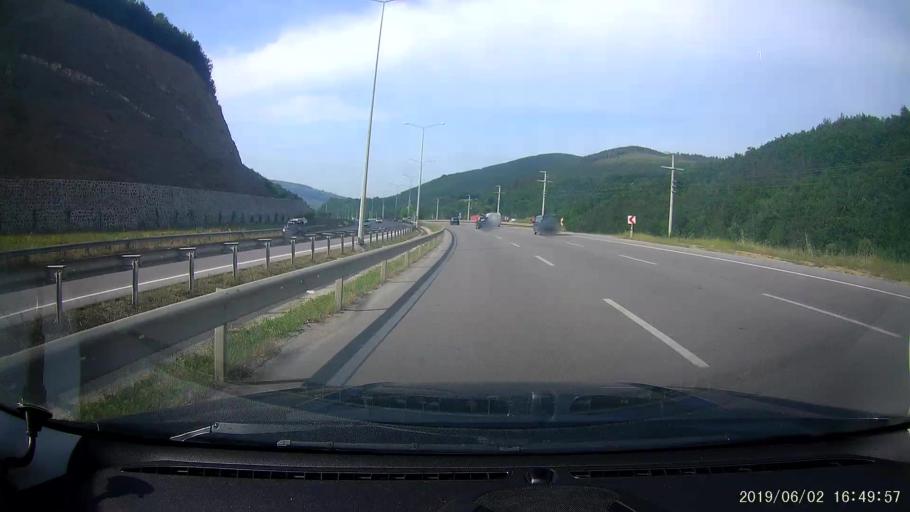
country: TR
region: Samsun
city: Samsun
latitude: 41.2445
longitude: 36.1716
